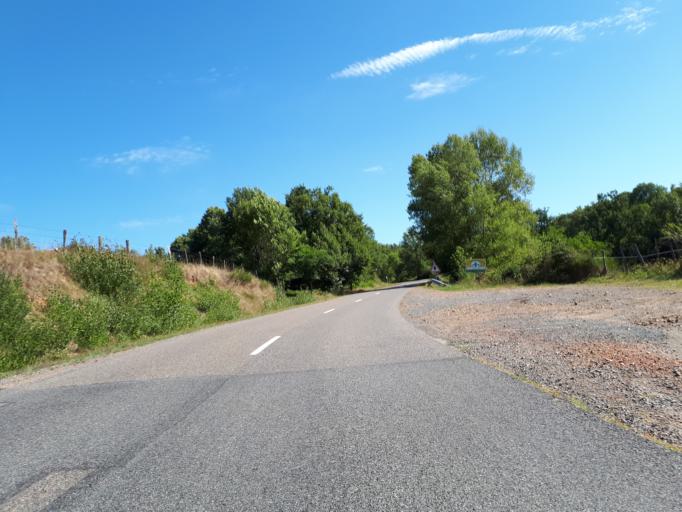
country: FR
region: Rhone-Alpes
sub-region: Departement de la Loire
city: Bussieres
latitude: 45.8248
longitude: 4.2528
